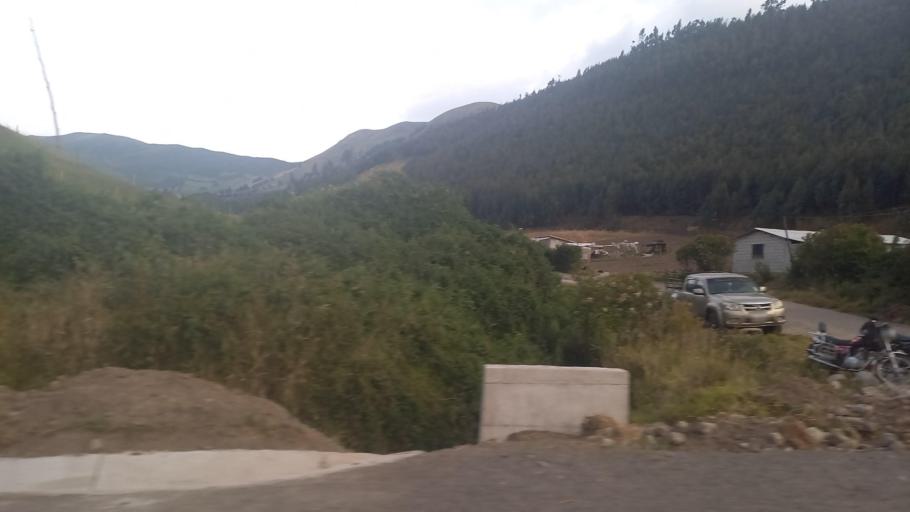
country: EC
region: Pichincha
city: Cayambe
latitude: 0.1283
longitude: -78.0699
